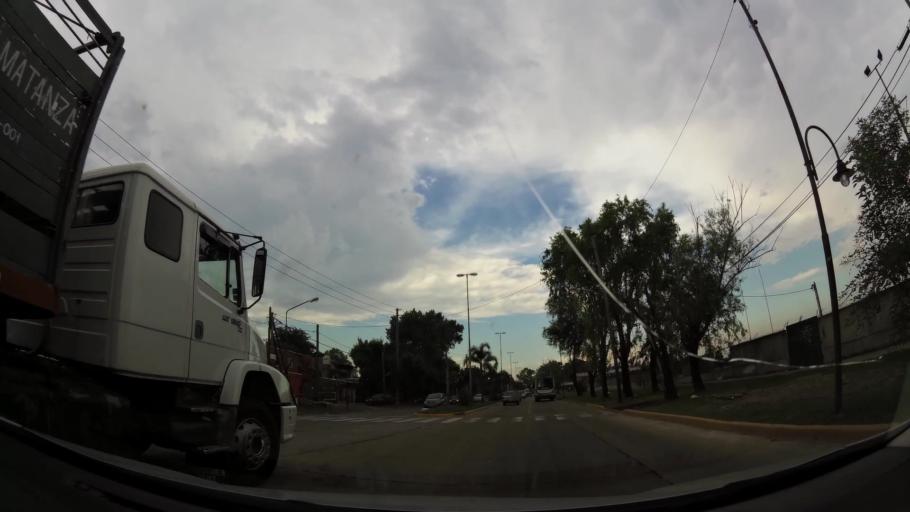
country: AR
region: Buenos Aires
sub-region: Partido de Tigre
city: Tigre
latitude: -34.4785
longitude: -58.6008
